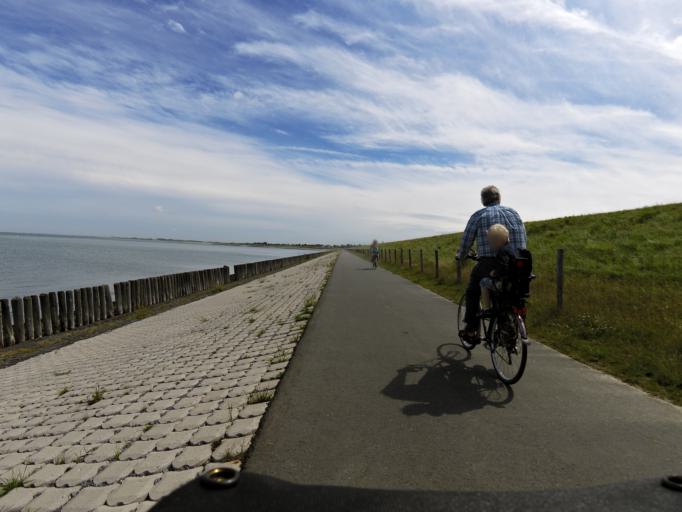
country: NL
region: Zeeland
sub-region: Gemeente Noord-Beveland
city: Kamperland
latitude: 51.5979
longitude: 3.7005
